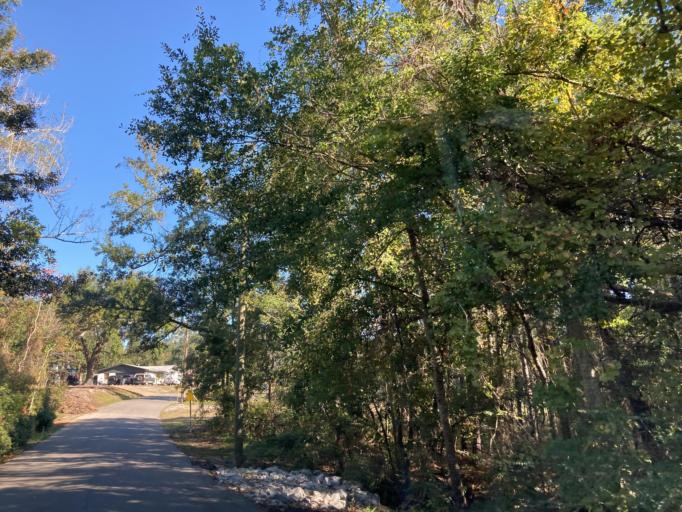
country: US
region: Mississippi
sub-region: Jackson County
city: Ocean Springs
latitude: 30.4155
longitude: -88.8368
